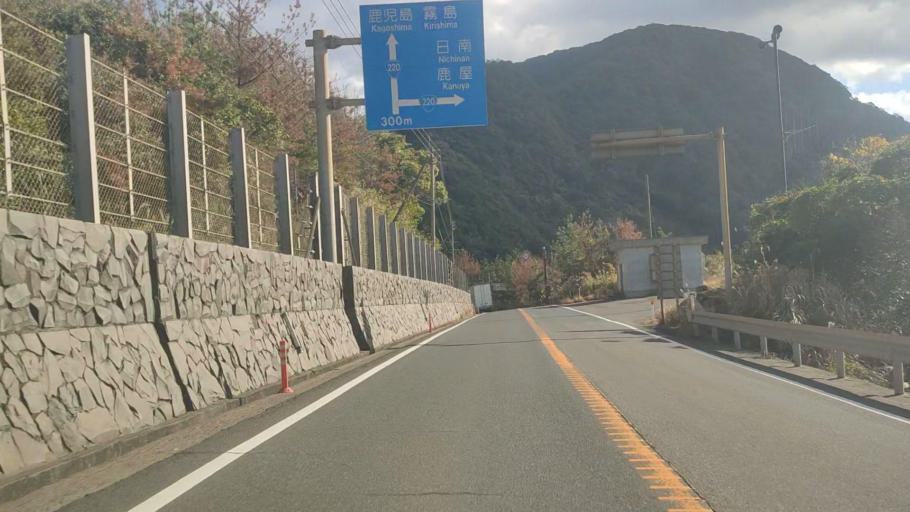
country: JP
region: Kagoshima
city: Tarumizu
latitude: 31.5559
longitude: 130.6955
